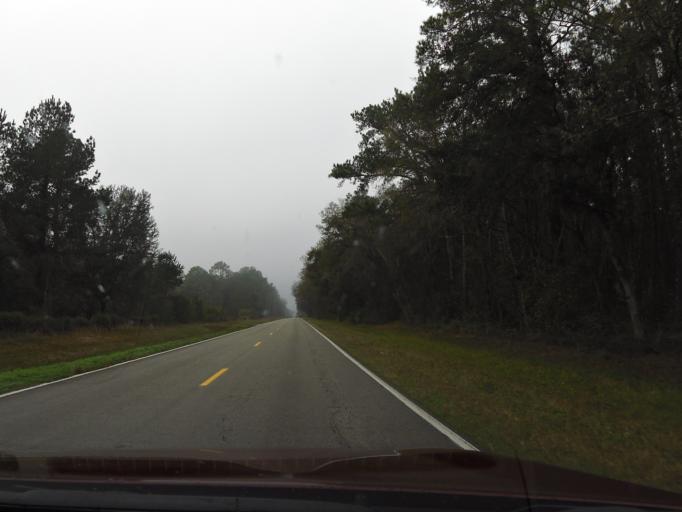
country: US
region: Florida
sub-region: Alachua County
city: High Springs
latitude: 29.8800
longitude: -82.4862
